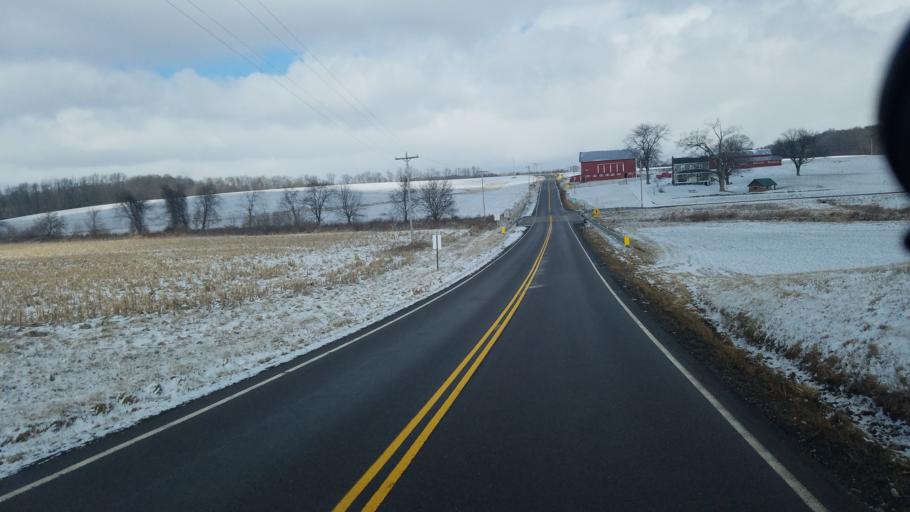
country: US
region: Ohio
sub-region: Knox County
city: Fredericktown
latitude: 40.5484
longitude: -82.5609
